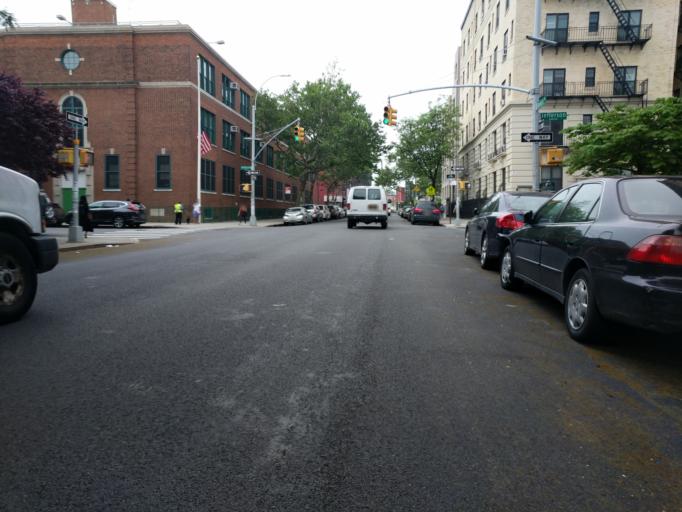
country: US
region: New York
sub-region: Kings County
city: Brooklyn
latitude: 40.6828
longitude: -73.9560
